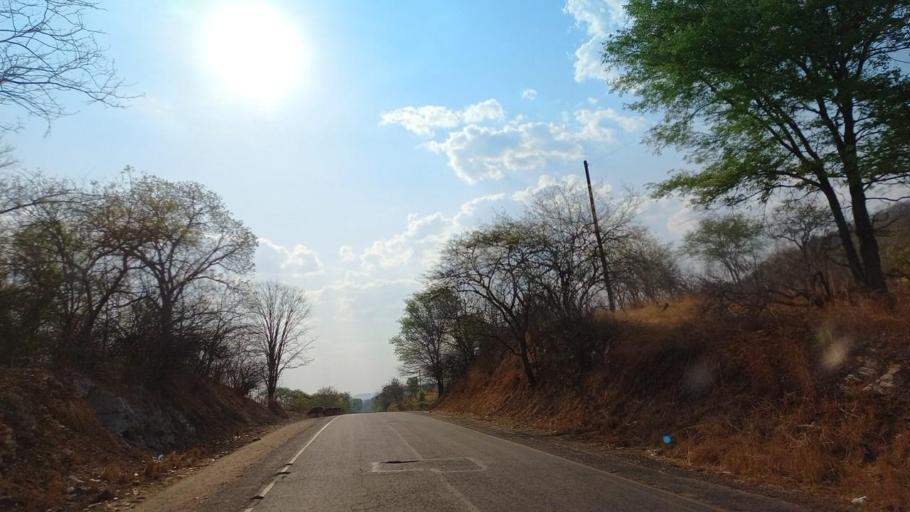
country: ZM
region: Lusaka
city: Luangwa
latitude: -14.9825
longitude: 30.1741
